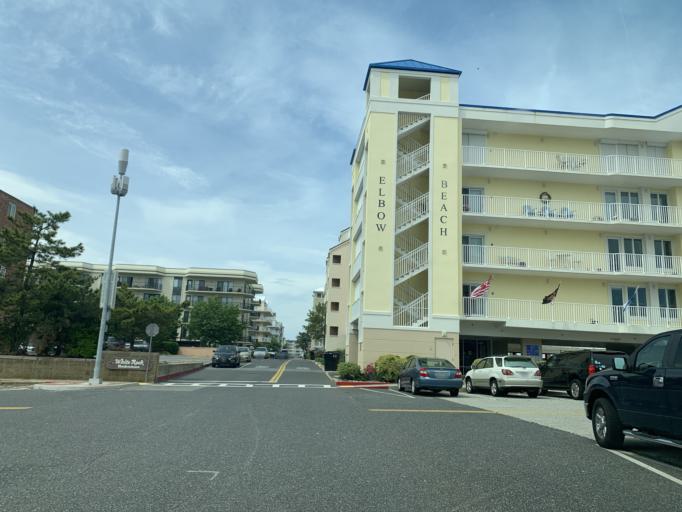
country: US
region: Delaware
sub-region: Sussex County
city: Bethany Beach
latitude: 38.4461
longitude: -75.0508
